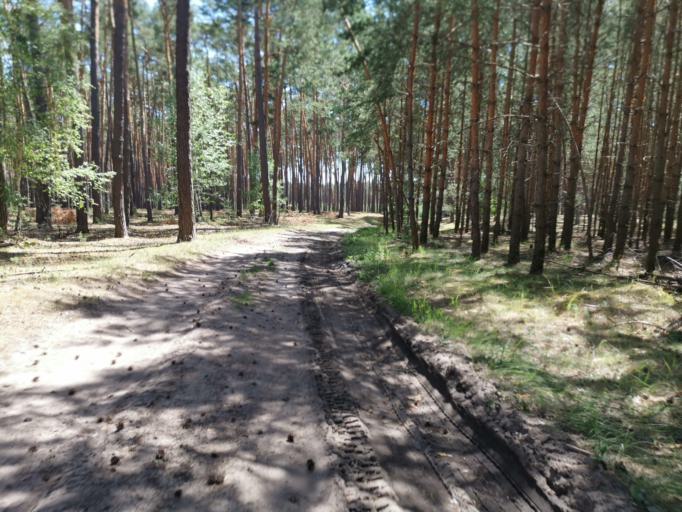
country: CZ
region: South Moravian
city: Vracov
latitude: 48.9659
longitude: 17.2210
